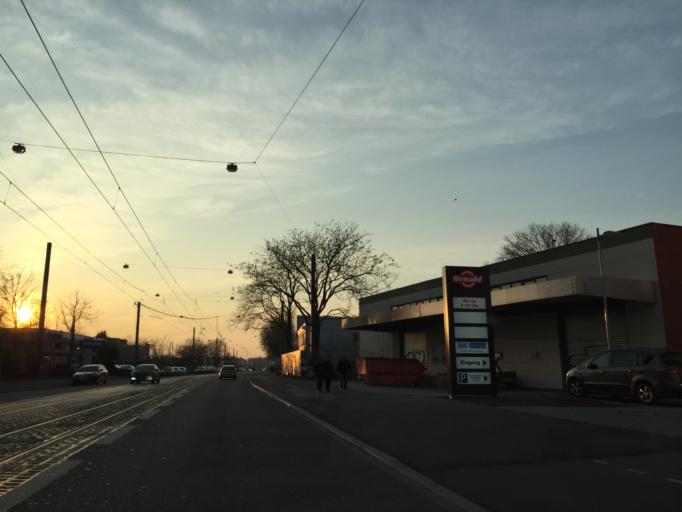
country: DE
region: Baden-Wuerttemberg
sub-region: Karlsruhe Region
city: Heidelberg
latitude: 49.4056
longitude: 8.6645
